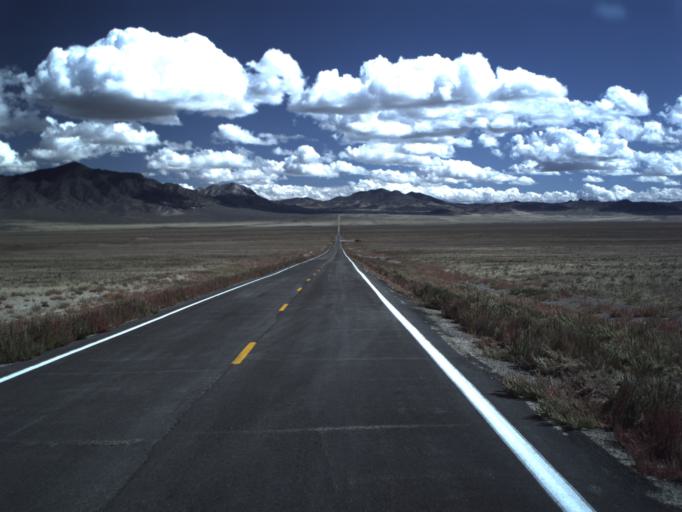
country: US
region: Utah
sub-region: Beaver County
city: Milford
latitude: 38.4837
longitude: -113.4477
